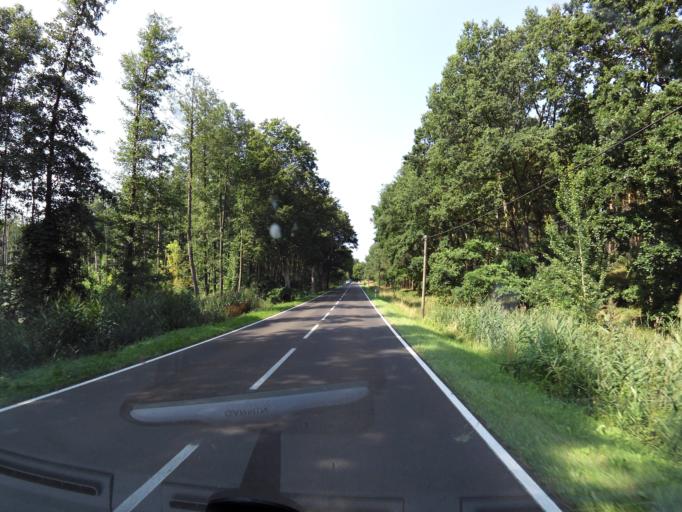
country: DE
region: Brandenburg
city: Liebenwalde
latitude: 52.9084
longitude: 13.3874
